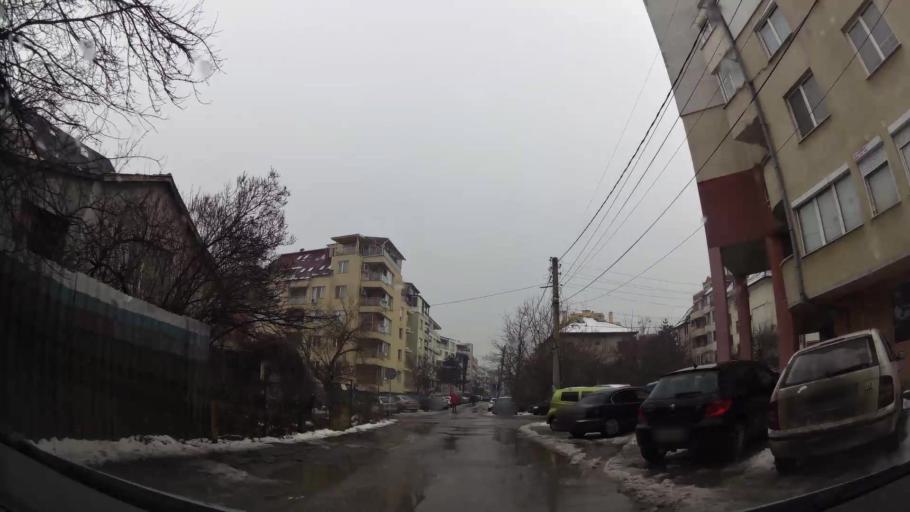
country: BG
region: Sofia-Capital
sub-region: Stolichna Obshtina
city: Sofia
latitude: 42.6623
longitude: 23.2780
